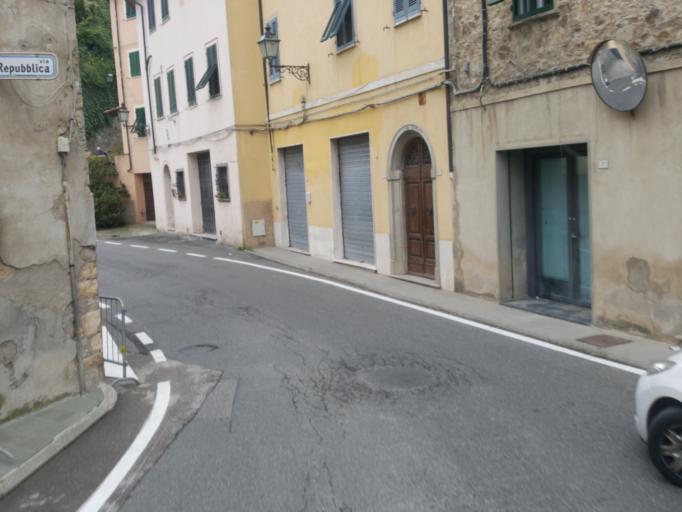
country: IT
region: Tuscany
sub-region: Province of Pisa
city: Castelnuovo di Val di Cecina
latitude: 43.2082
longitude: 10.9058
